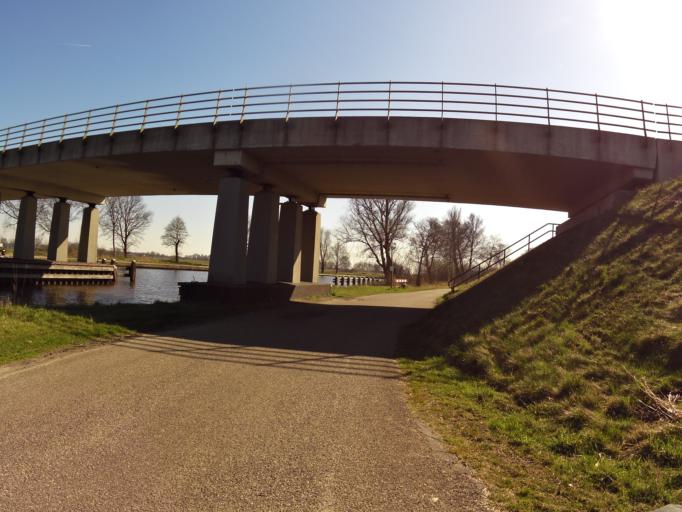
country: NL
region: Overijssel
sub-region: Gemeente Steenwijkerland
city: Blokzijl
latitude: 52.7447
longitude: 5.9960
